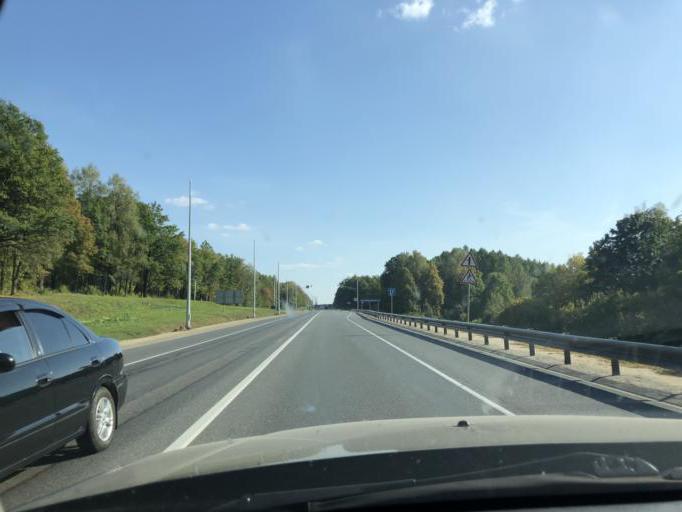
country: RU
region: Tula
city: Gorelki
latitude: 54.3222
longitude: 37.5589
